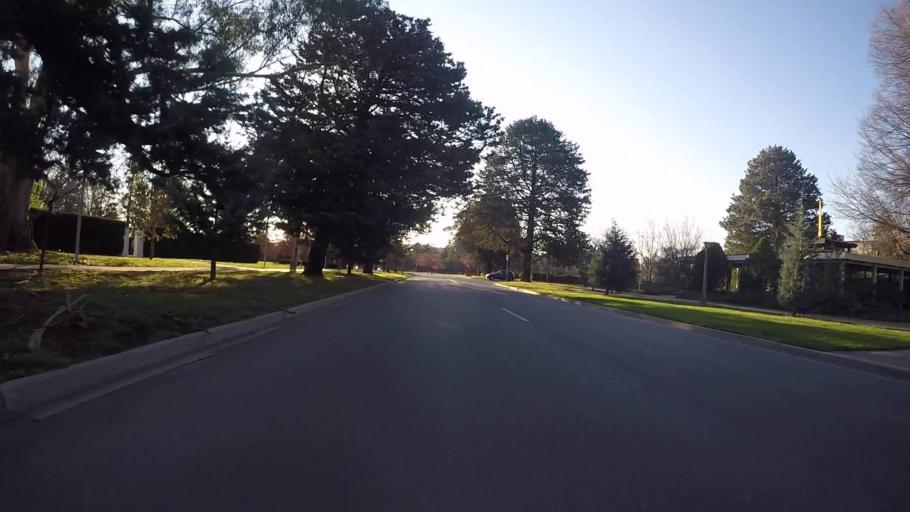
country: AU
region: Australian Capital Territory
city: Forrest
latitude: -35.3008
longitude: 149.1287
